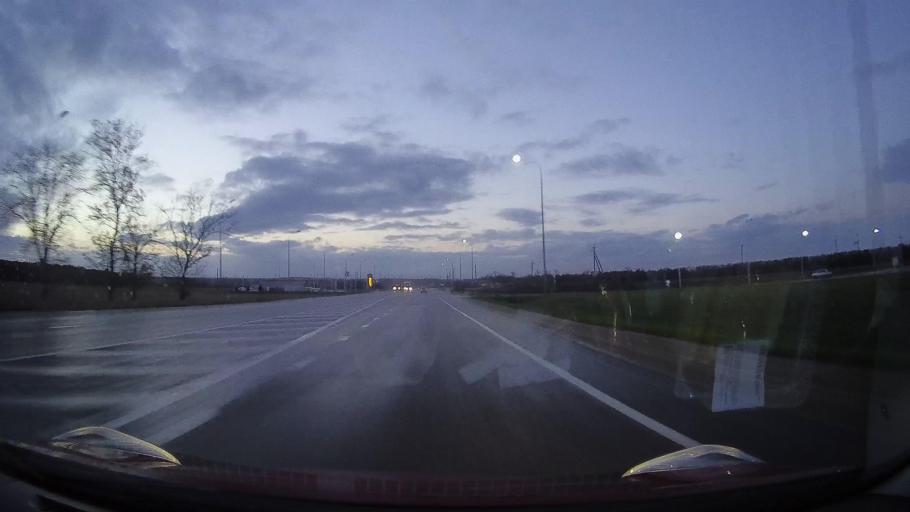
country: RU
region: Krasnodarskiy
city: Zavetnyy
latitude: 44.9088
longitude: 41.1680
